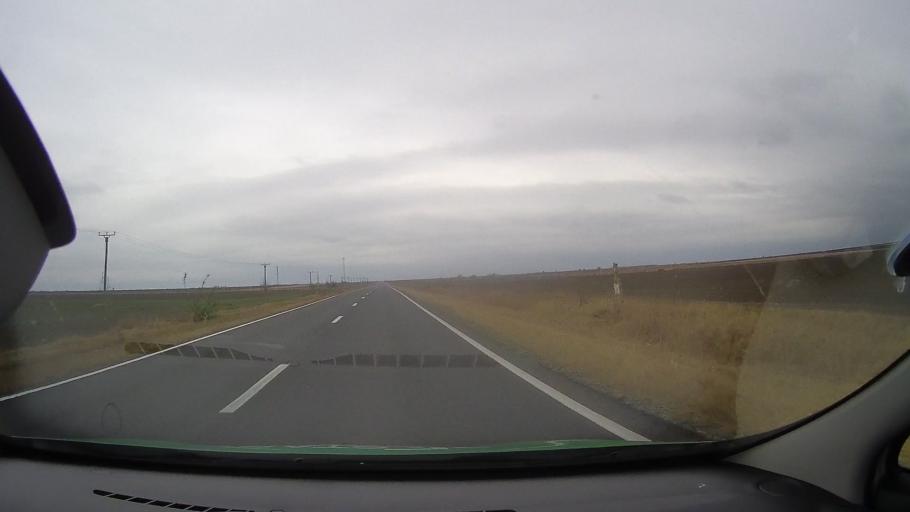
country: RO
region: Constanta
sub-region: Comuna Nicolae Balcescu
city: Nicolae Balcescu
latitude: 44.3773
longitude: 28.4176
